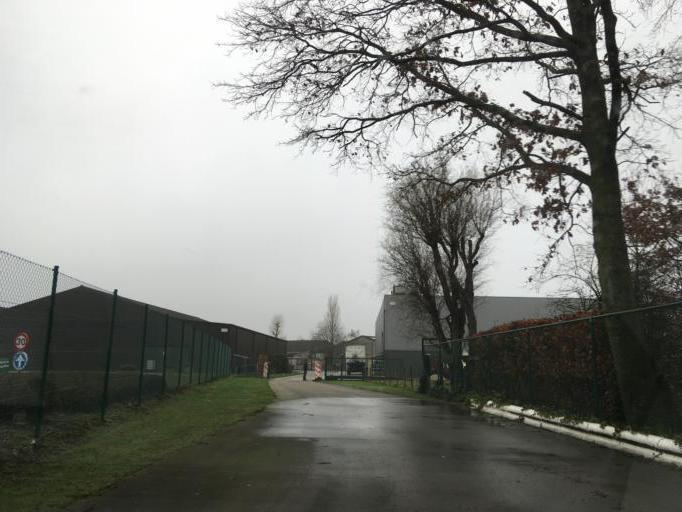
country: BE
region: Flanders
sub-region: Provincie West-Vlaanderen
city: Roeselare
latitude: 50.9716
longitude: 3.1528
